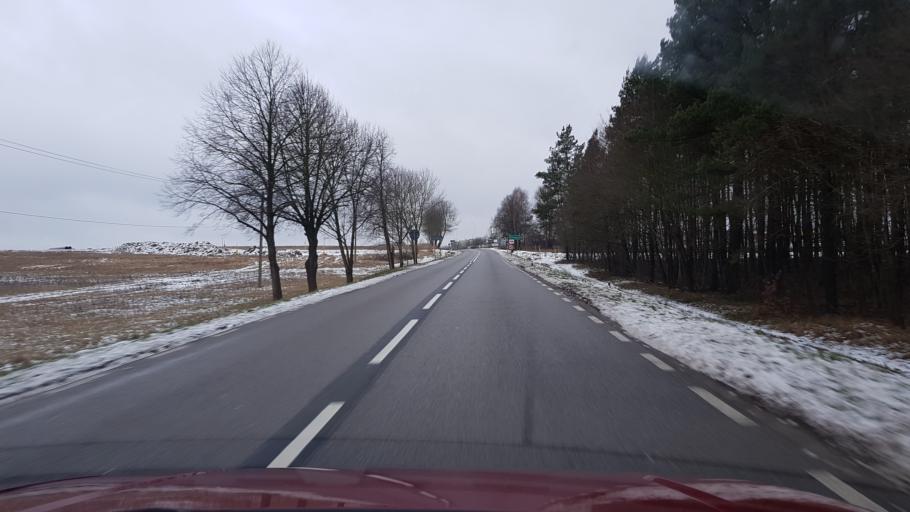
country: PL
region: West Pomeranian Voivodeship
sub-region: Powiat goleniowski
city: Nowogard
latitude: 53.6618
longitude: 15.1627
